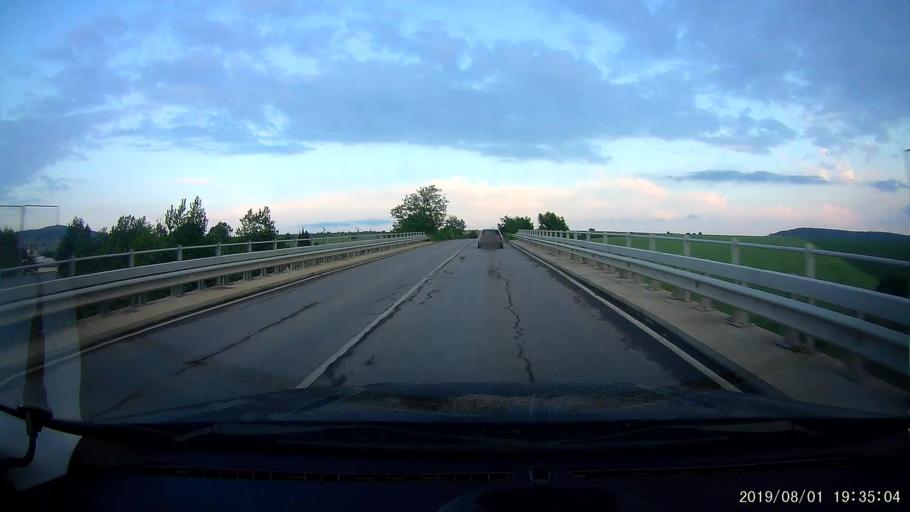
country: BG
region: Burgas
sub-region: Obshtina Sungurlare
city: Sungurlare
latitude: 42.7650
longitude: 26.8810
